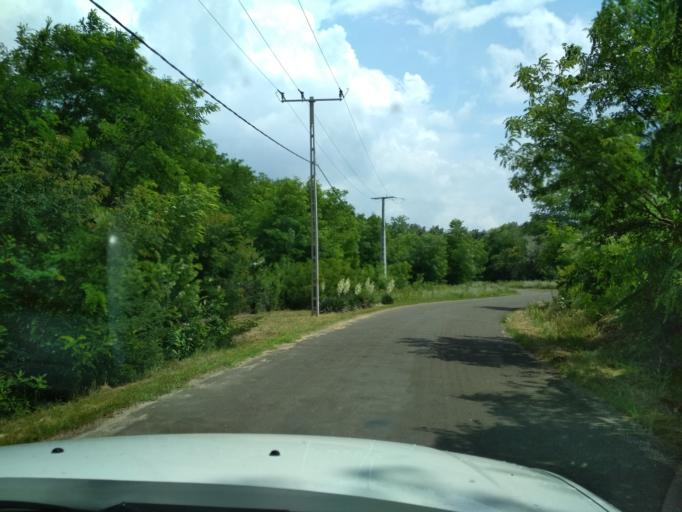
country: HU
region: Pest
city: Nagykata
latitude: 47.3818
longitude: 19.7580
